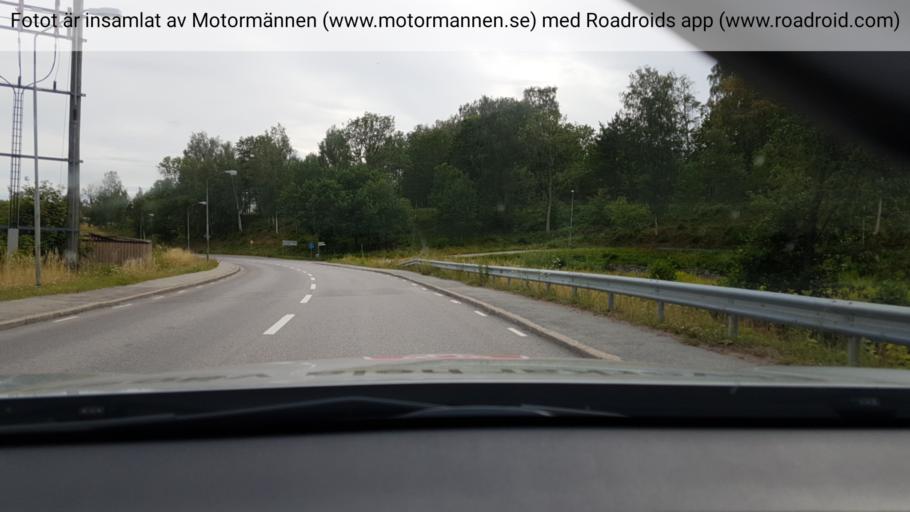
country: SE
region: Vaestra Goetaland
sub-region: Bengtsfors Kommun
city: Billingsfors
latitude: 58.9890
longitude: 12.2538
